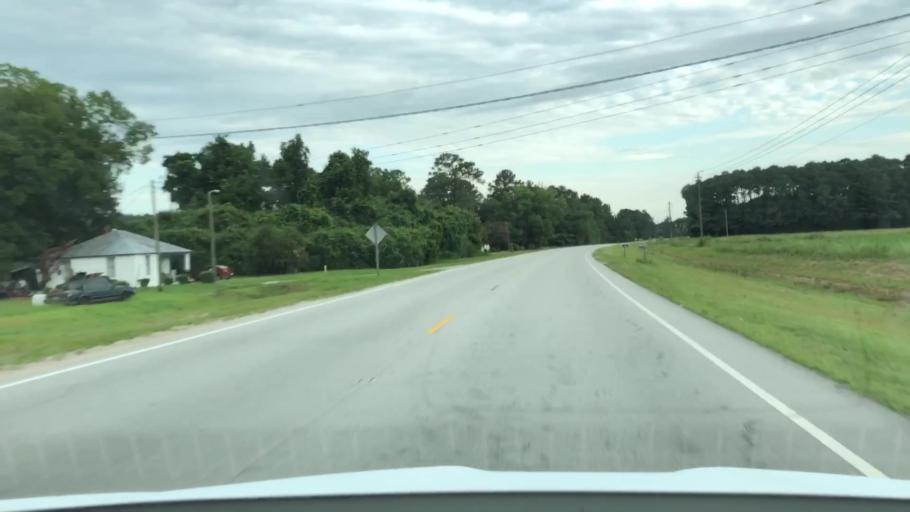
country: US
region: North Carolina
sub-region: Jones County
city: Trenton
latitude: 35.0200
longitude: -77.3031
